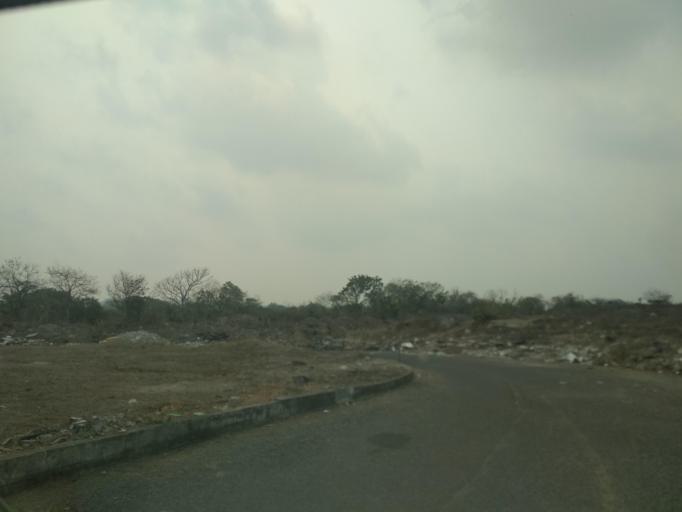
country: MX
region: Veracruz
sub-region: Veracruz
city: Fraccionamiento Geovillas los Pinos
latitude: 19.2295
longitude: -96.2413
